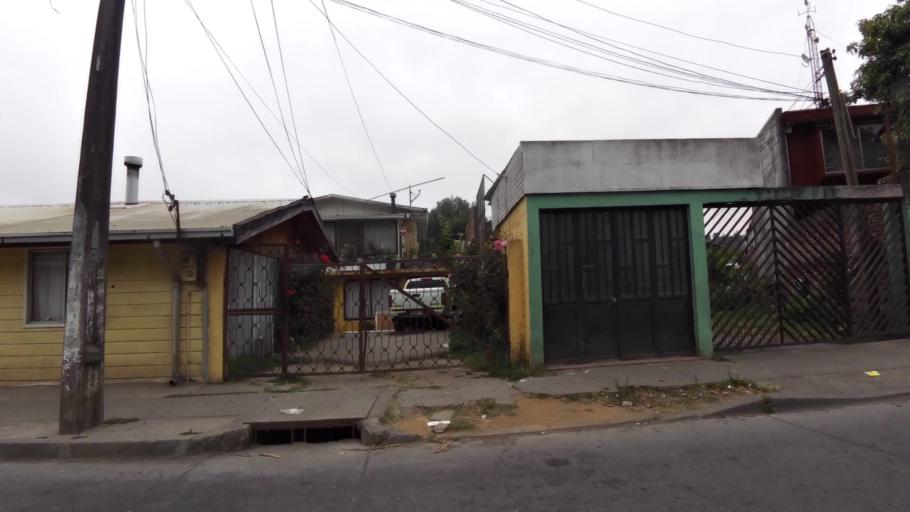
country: CL
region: Biobio
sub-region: Provincia de Concepcion
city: Concepcion
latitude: -36.8365
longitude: -73.0014
